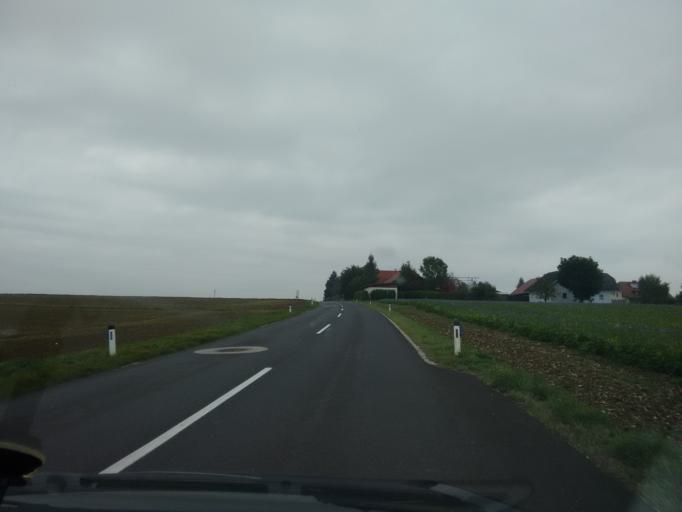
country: AT
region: Upper Austria
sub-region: Politischer Bezirk Kirchdorf an der Krems
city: Kremsmunster
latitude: 48.0337
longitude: 14.0893
